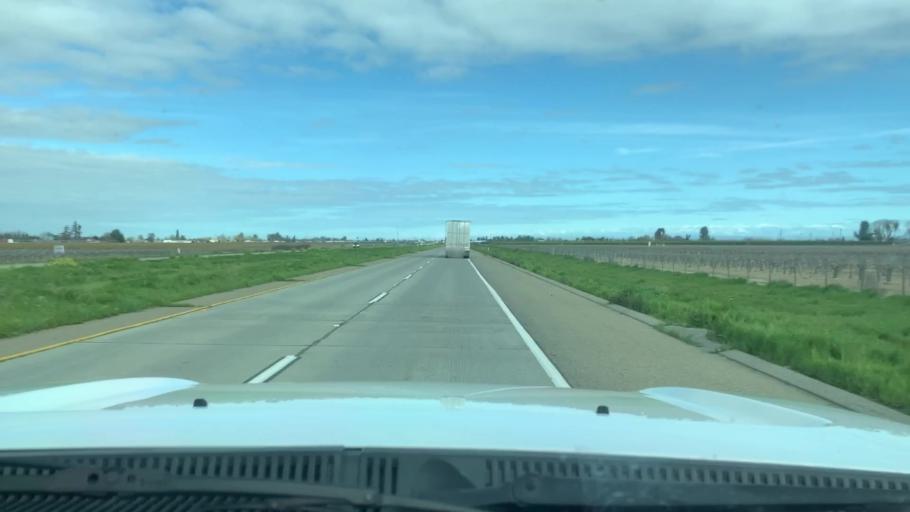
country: US
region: California
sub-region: Fresno County
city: Easton
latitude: 36.5958
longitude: -119.7855
